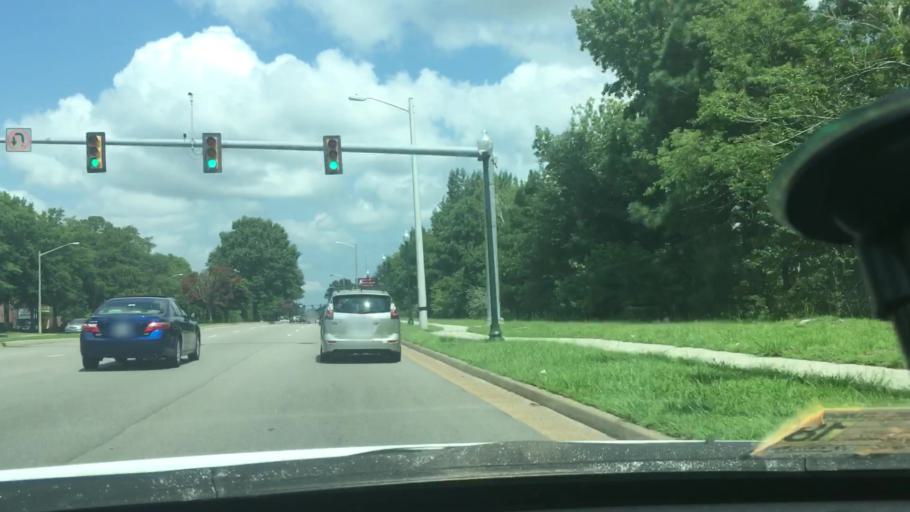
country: US
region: Virginia
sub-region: City of Chesapeake
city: Chesapeake
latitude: 36.7715
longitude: -76.2284
